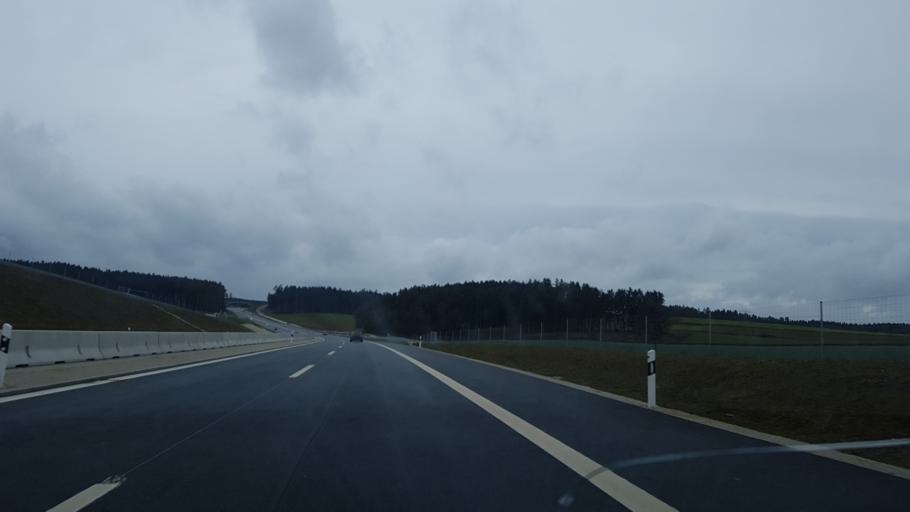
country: DE
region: Bavaria
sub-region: Lower Bavaria
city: Essenbach
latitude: 48.6433
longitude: 12.2005
